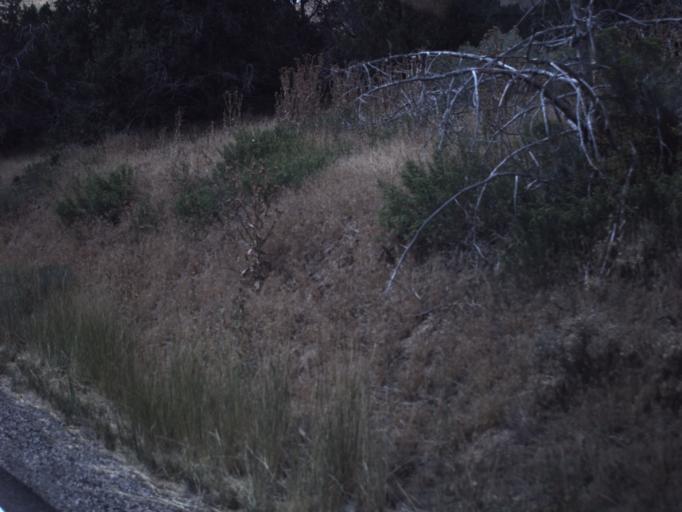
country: US
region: Utah
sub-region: Tooele County
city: Grantsville
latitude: 40.3451
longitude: -112.5859
